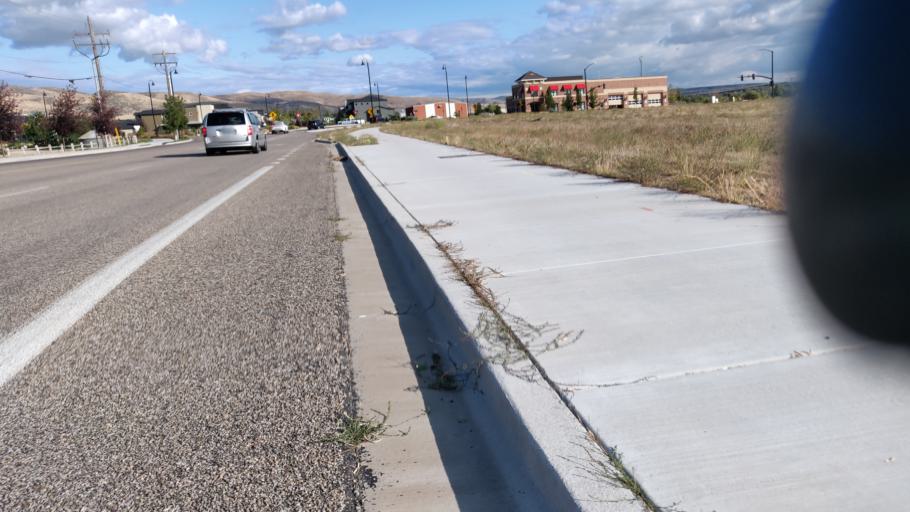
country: US
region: Idaho
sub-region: Ada County
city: Boise
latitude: 43.5771
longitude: -116.1416
